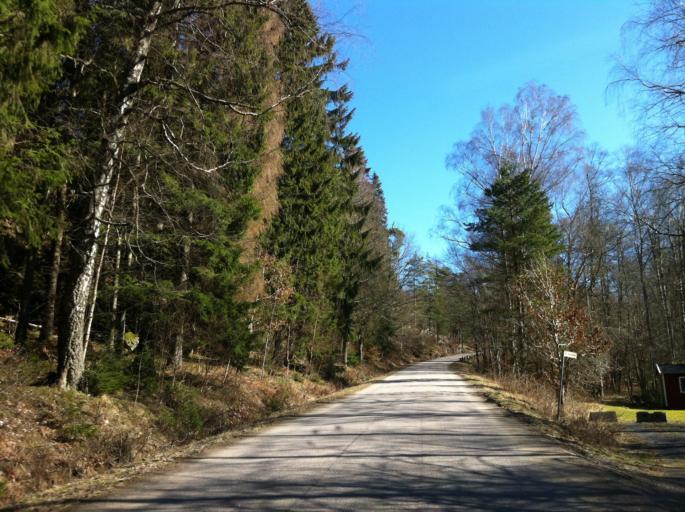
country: SE
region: Vaestra Goetaland
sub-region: Vanersborgs Kommun
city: Vargon
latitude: 58.3534
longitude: 12.4064
